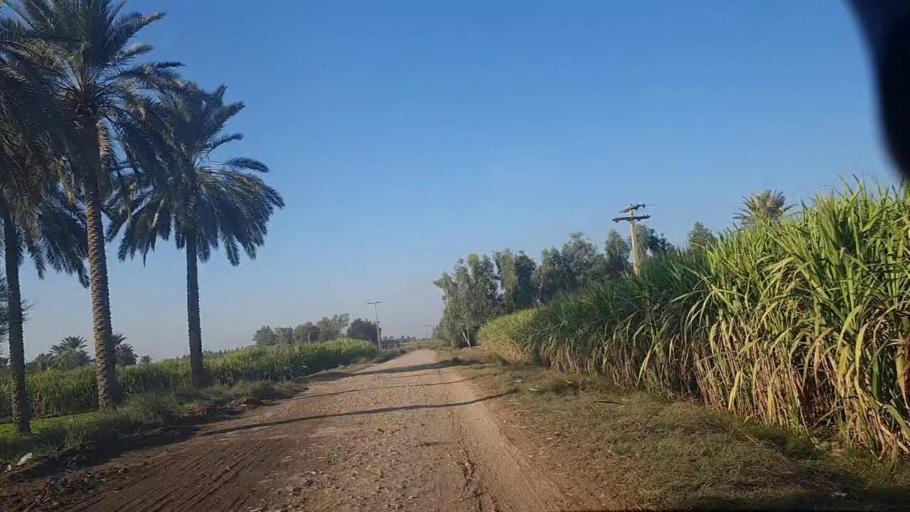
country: PK
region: Sindh
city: Sobhadero
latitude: 27.3951
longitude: 68.4197
